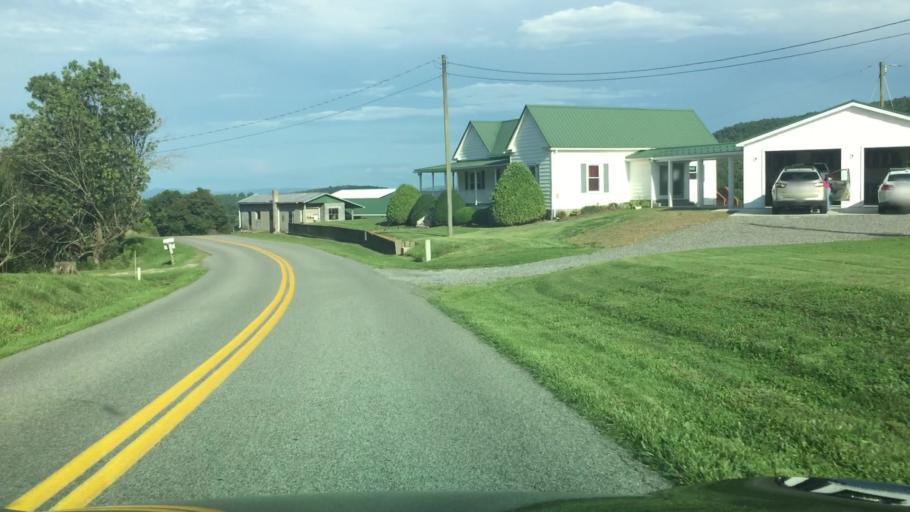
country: US
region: Virginia
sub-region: Wythe County
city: Wytheville
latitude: 36.9395
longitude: -80.9660
